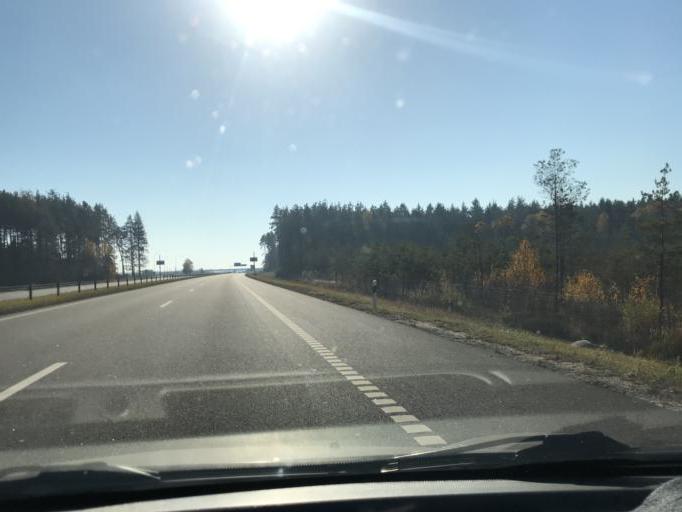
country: BY
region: Mogilev
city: Babruysk
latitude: 53.1945
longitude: 29.3519
